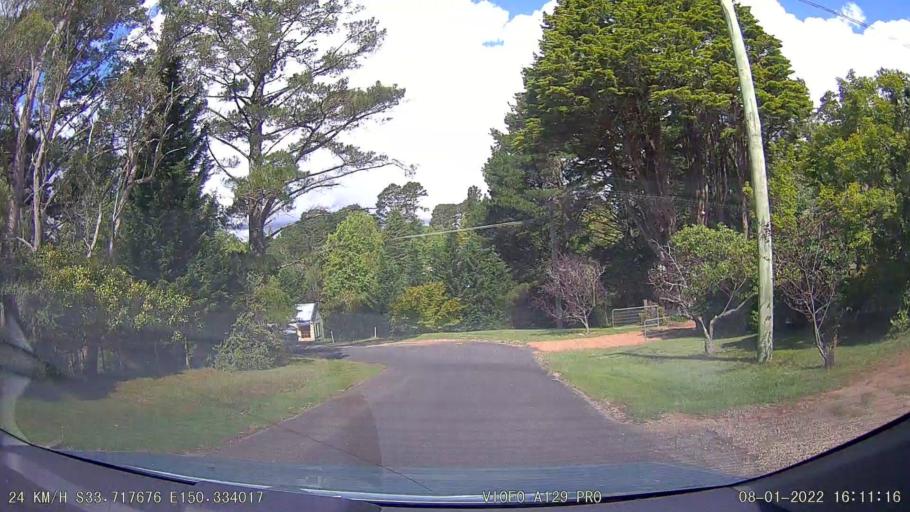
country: AU
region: New South Wales
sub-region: Blue Mountains Municipality
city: Leura
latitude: -33.7177
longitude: 150.3340
